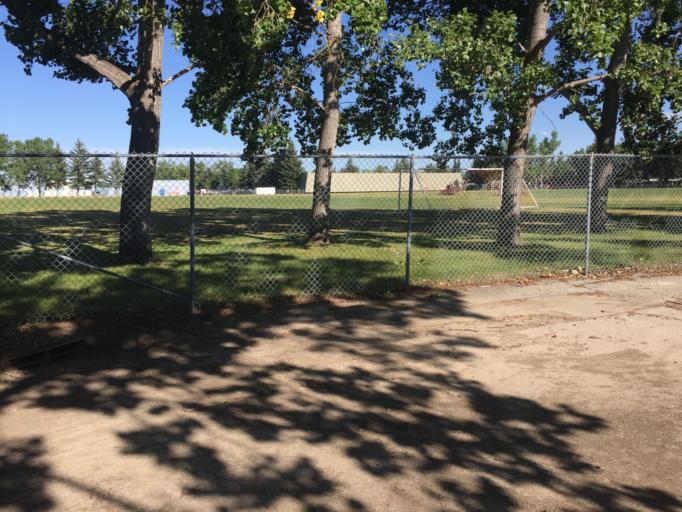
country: CA
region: Alberta
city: Calgary
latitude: 50.9370
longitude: -114.0529
